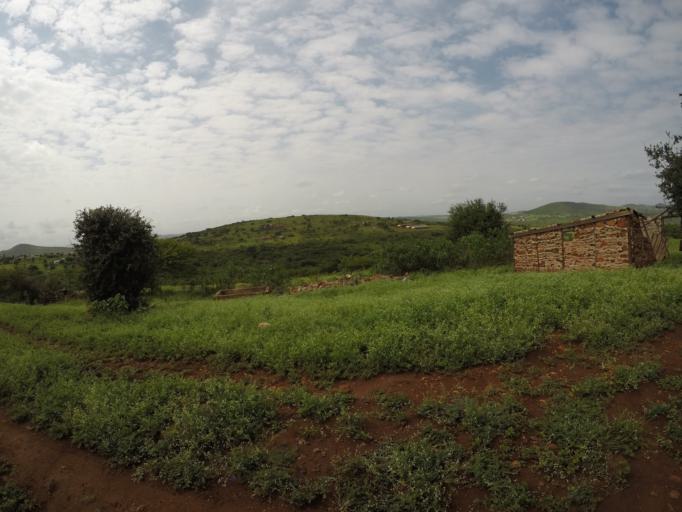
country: ZA
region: KwaZulu-Natal
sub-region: uThungulu District Municipality
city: Empangeni
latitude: -28.6190
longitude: 31.8982
